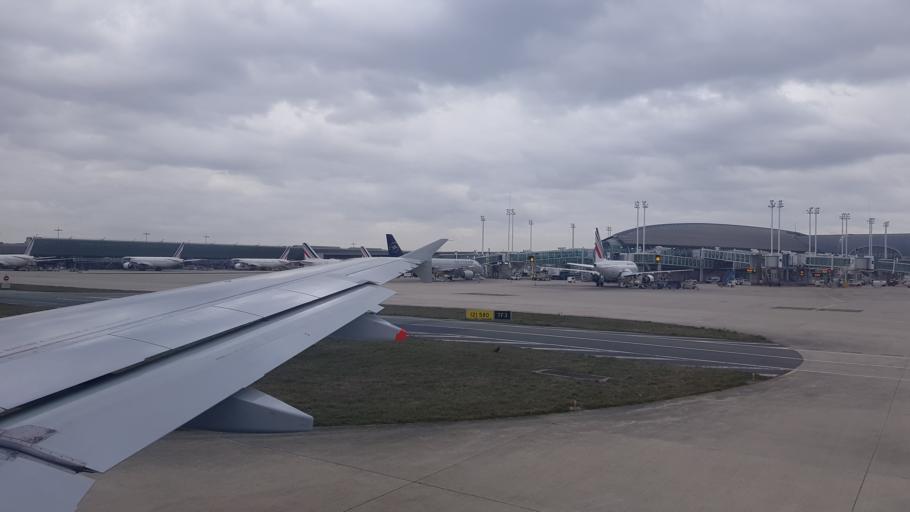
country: FR
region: Ile-de-France
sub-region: Departement de Seine-et-Marne
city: Mitry-Mory
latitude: 49.0084
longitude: 2.5775
